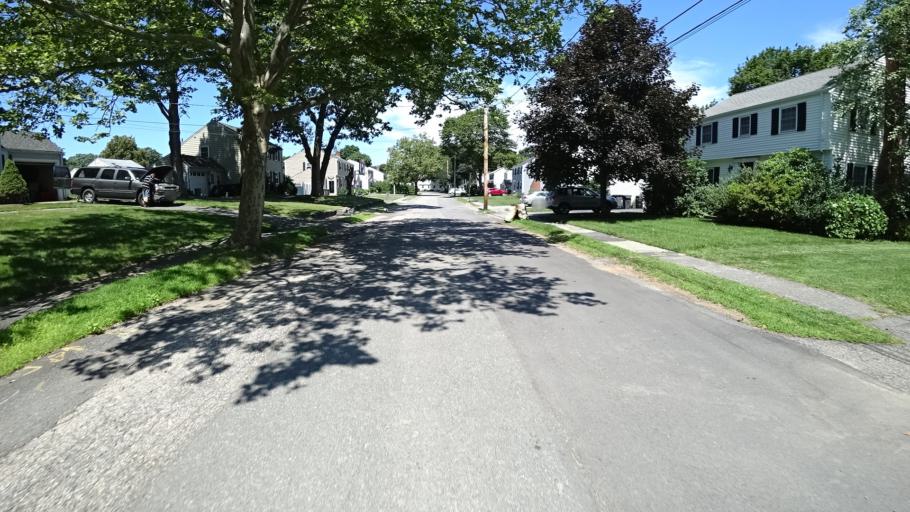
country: US
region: Massachusetts
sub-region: Norfolk County
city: Dedham
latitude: 42.2352
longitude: -71.1543
